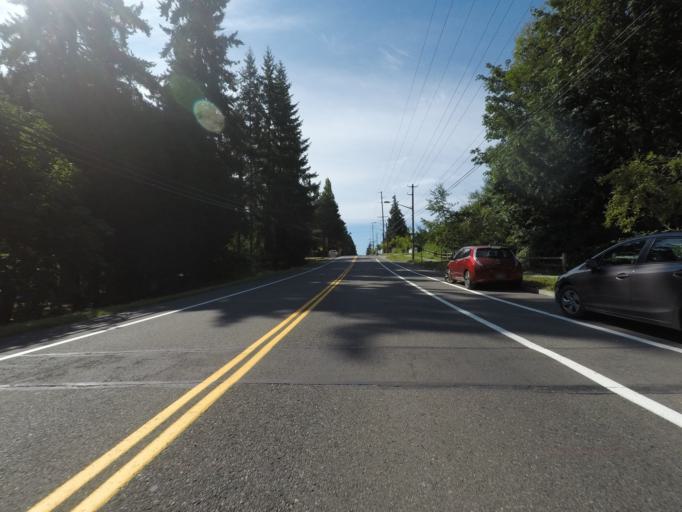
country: US
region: Washington
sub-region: King County
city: Inglewood-Finn Hill
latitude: 47.7215
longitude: -122.2294
